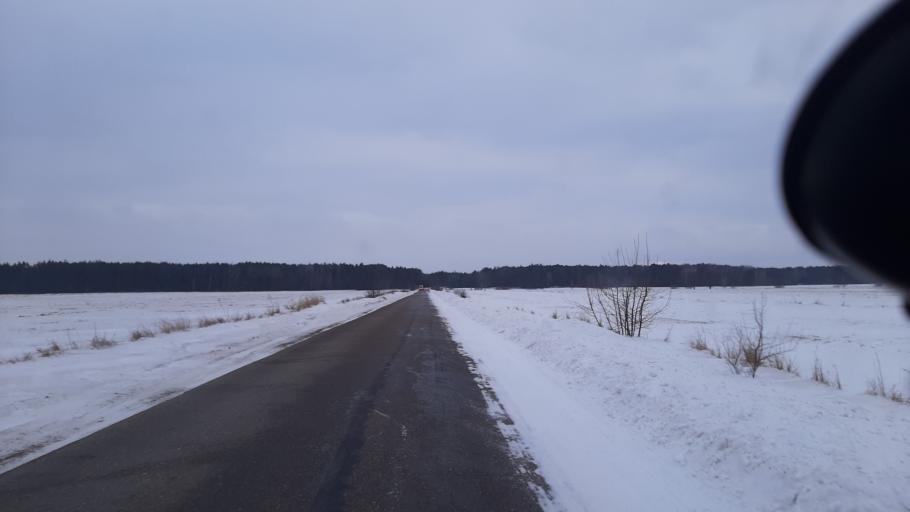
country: PL
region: Lublin Voivodeship
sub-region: Powiat lubartowski
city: Abramow
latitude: 51.4428
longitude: 22.2650
